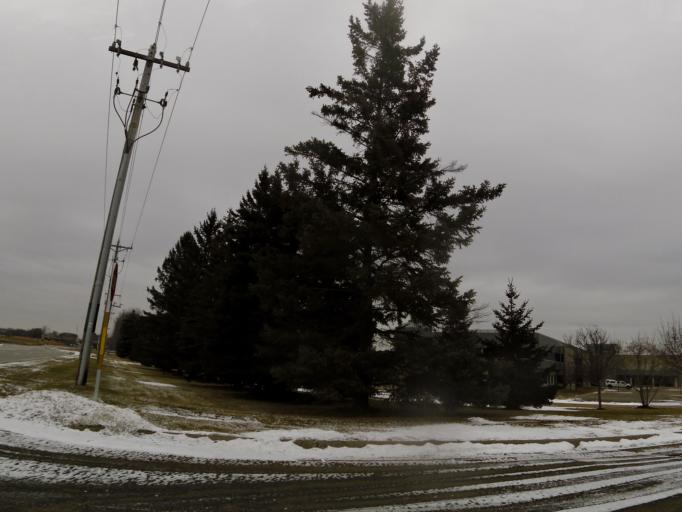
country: US
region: Minnesota
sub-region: Hennepin County
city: Medina
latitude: 45.0481
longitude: -93.5633
